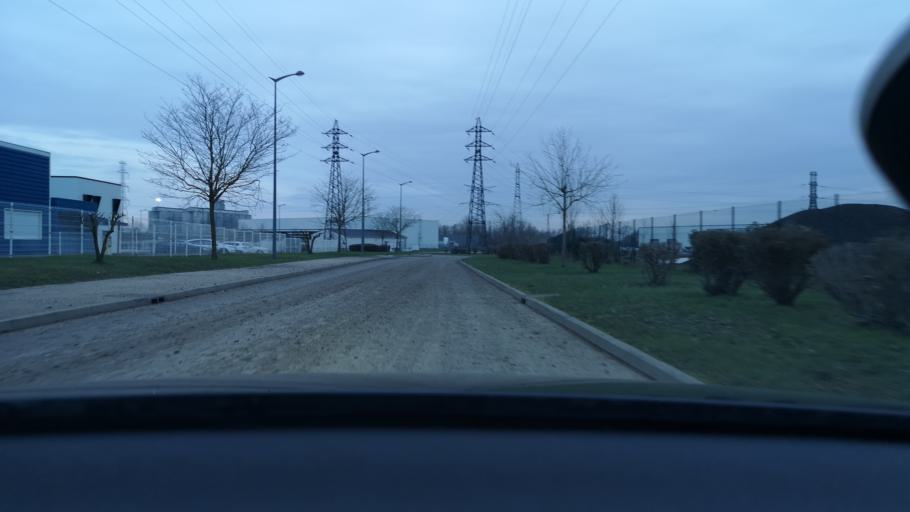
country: FR
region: Bourgogne
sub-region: Departement de Saone-et-Loire
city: Chalon-sur-Saone
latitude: 46.7656
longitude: 4.8667
